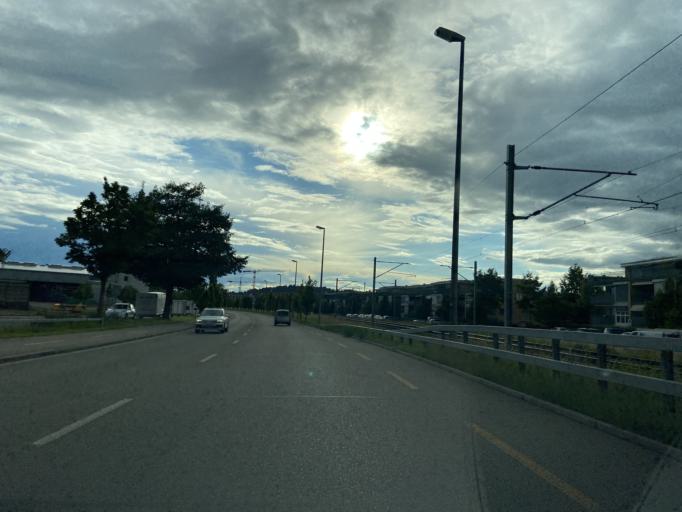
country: CH
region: Zurich
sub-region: Bezirk Winterthur
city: Oberwinterthur (Kreis 2) / Hegi
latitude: 47.5025
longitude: 8.7786
